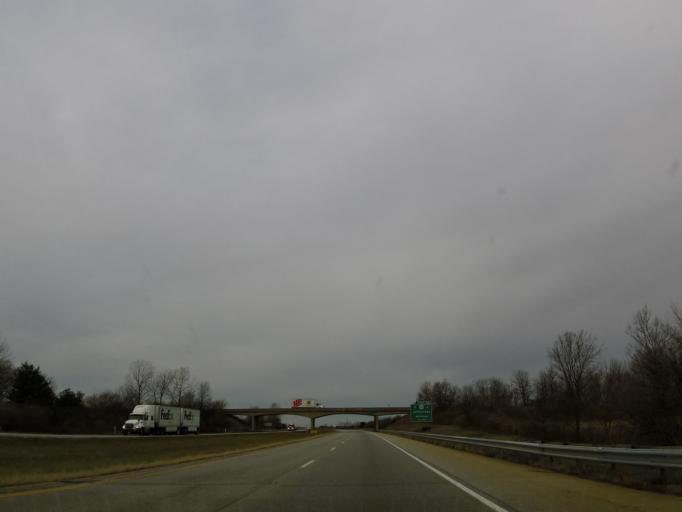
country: US
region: Indiana
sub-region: Hendricks County
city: Pittsboro
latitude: 39.9358
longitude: -86.6032
